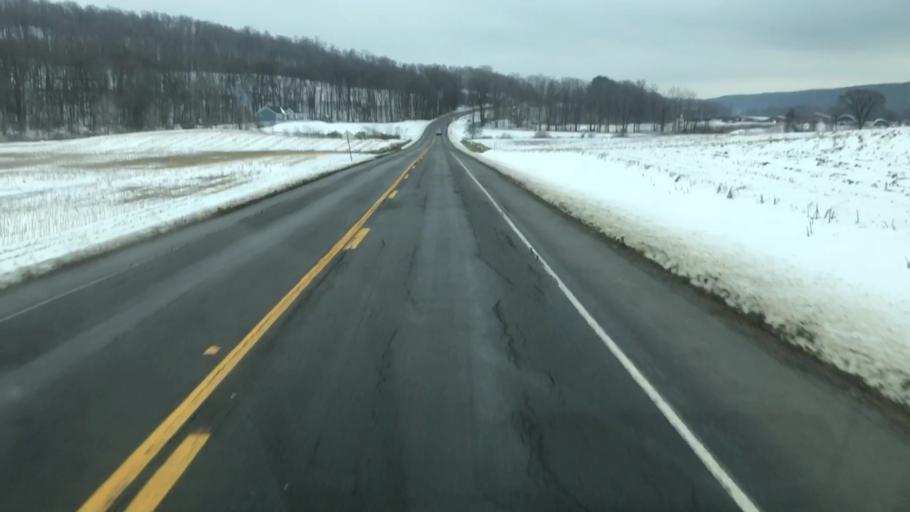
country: US
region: New York
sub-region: Cayuga County
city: Moravia
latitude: 42.7004
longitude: -76.3085
